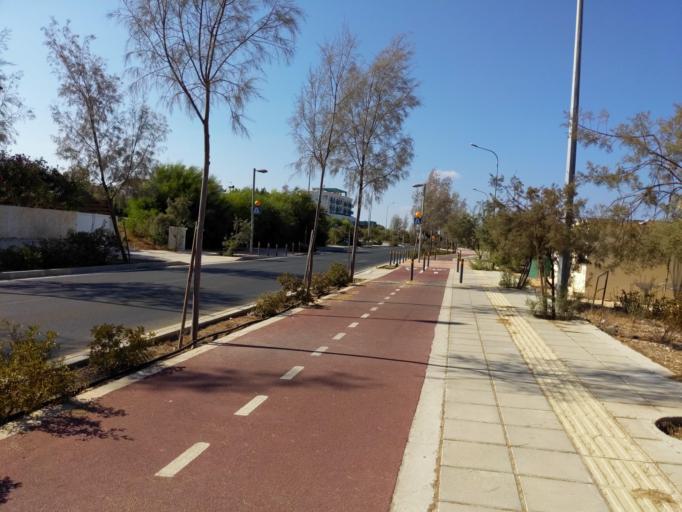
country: CY
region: Ammochostos
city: Protaras
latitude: 35.0280
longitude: 34.0387
